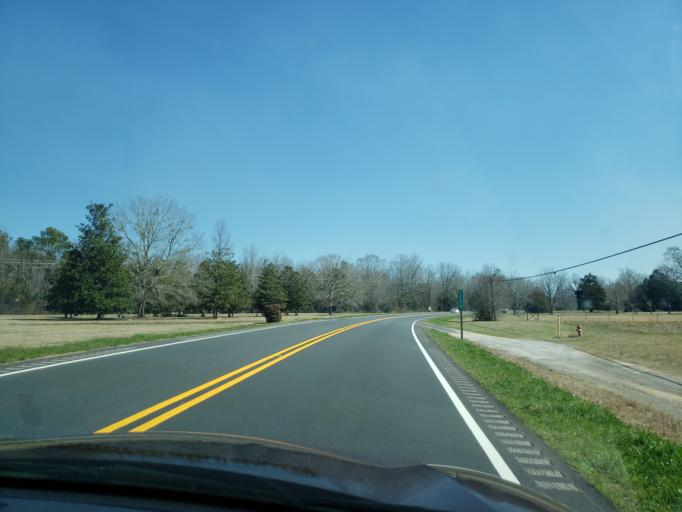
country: US
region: Alabama
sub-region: Macon County
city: Tuskegee
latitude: 32.5818
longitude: -85.7188
